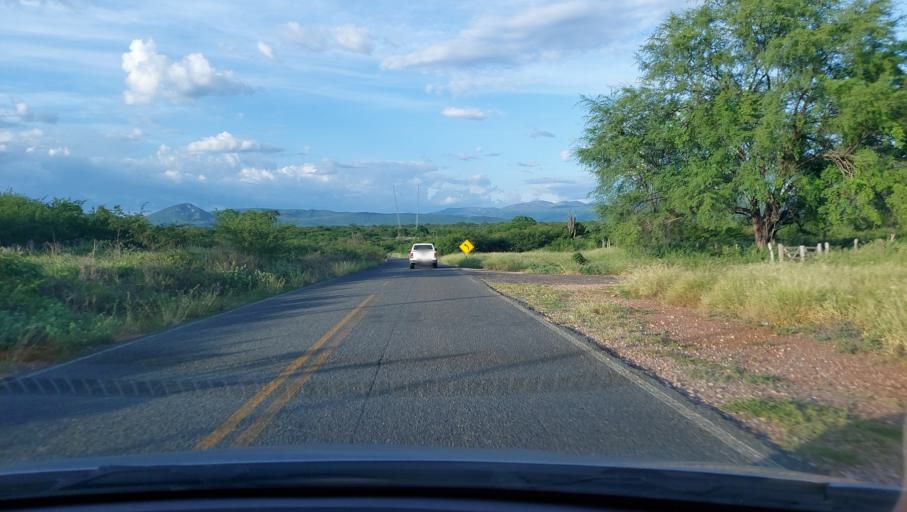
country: BR
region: Bahia
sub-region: Oliveira Dos Brejinhos
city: Beira Rio
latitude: -12.1973
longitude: -42.5376
